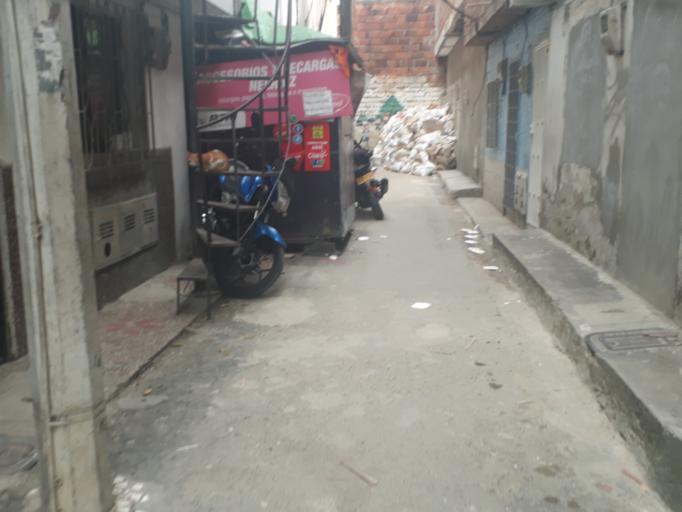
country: CO
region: Antioquia
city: Medellin
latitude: 6.2748
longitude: -75.5654
